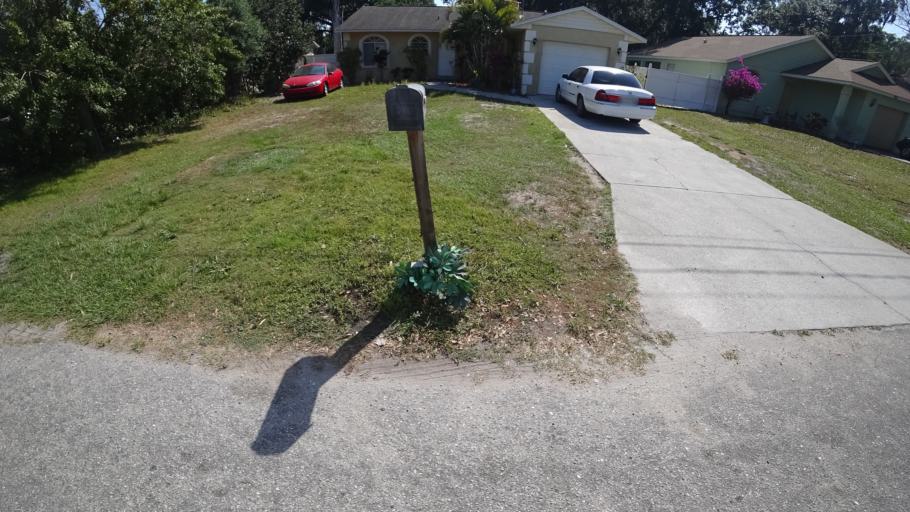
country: US
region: Florida
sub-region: Manatee County
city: Samoset
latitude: 27.4743
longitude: -82.5358
